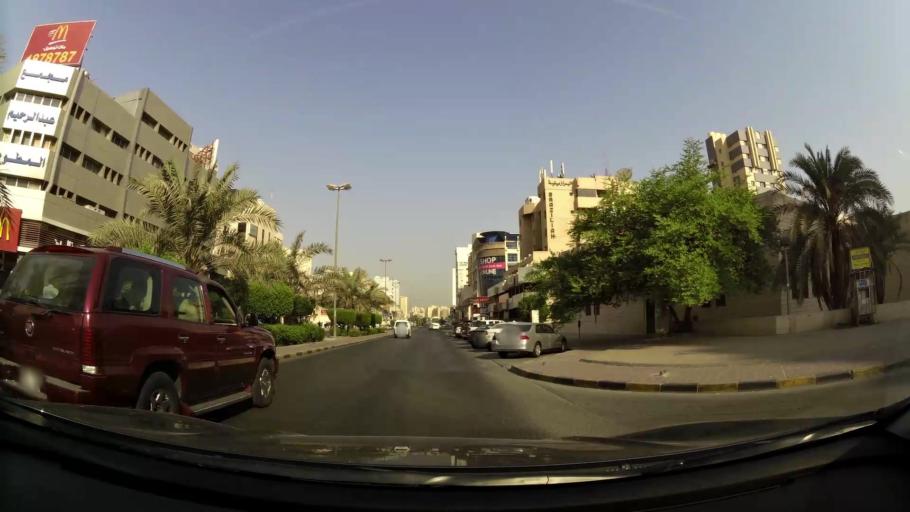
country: KW
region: Muhafazat Hawalli
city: Hawalli
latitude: 29.3326
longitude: 48.0270
